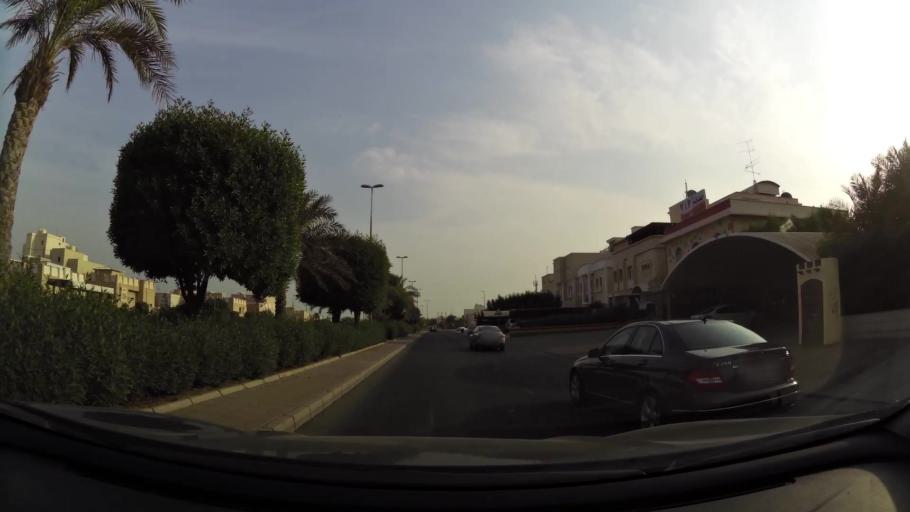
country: KW
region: Mubarak al Kabir
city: Mubarak al Kabir
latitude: 29.1868
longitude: 48.0717
